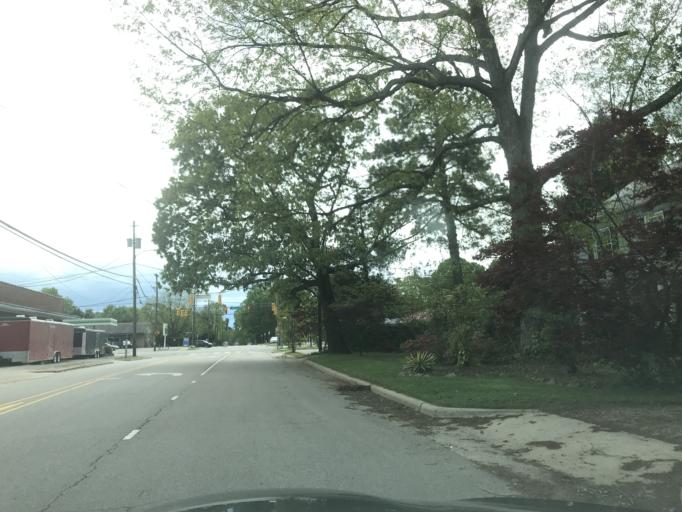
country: US
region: North Carolina
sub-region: Wake County
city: West Raleigh
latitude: 35.7873
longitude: -78.7127
